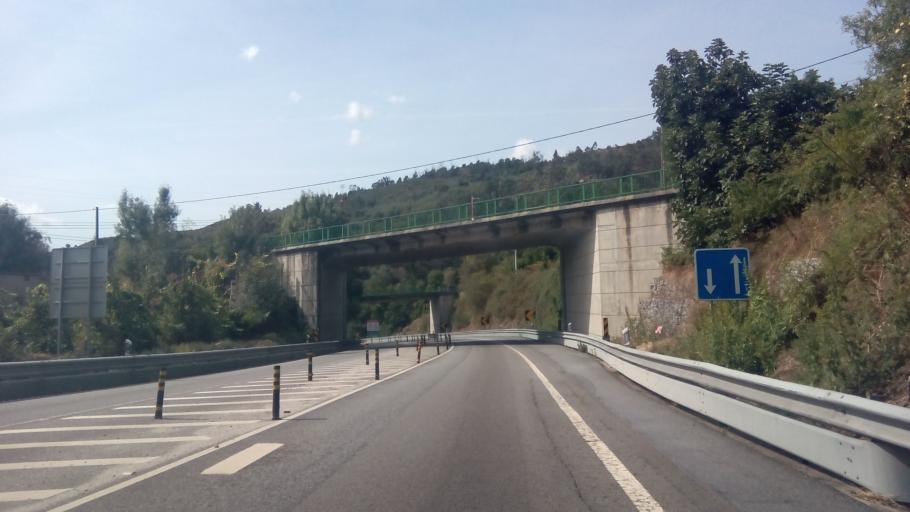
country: PT
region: Porto
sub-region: Amarante
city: Amarante
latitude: 41.2752
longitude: -8.0052
